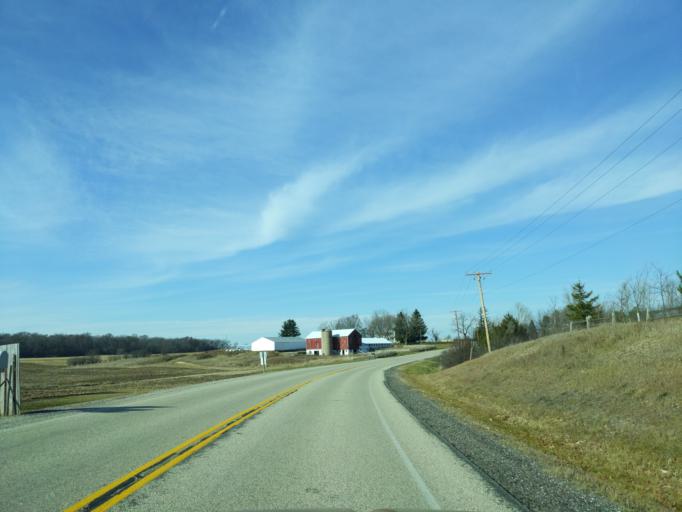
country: US
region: Wisconsin
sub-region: Walworth County
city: Elkhorn
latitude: 42.7547
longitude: -88.6011
